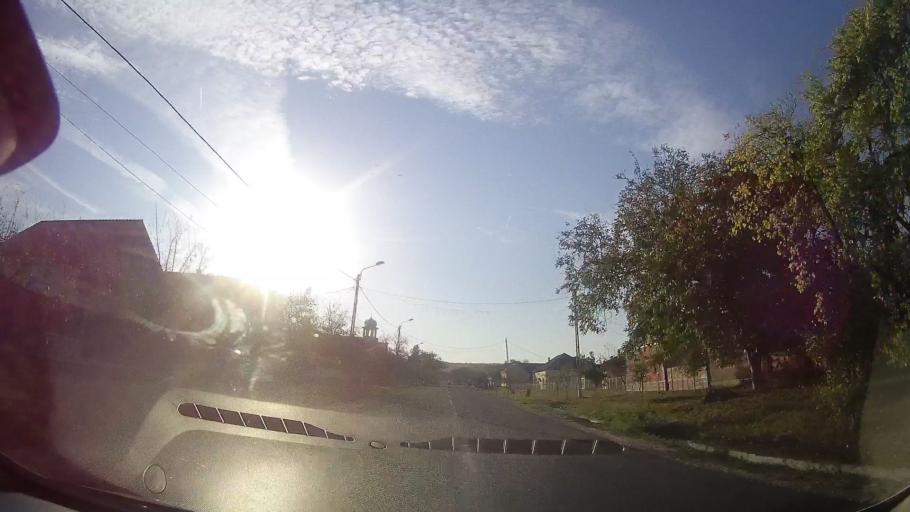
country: RO
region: Timis
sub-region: Comuna Masloc
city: Masloc
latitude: 45.9678
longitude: 21.4786
